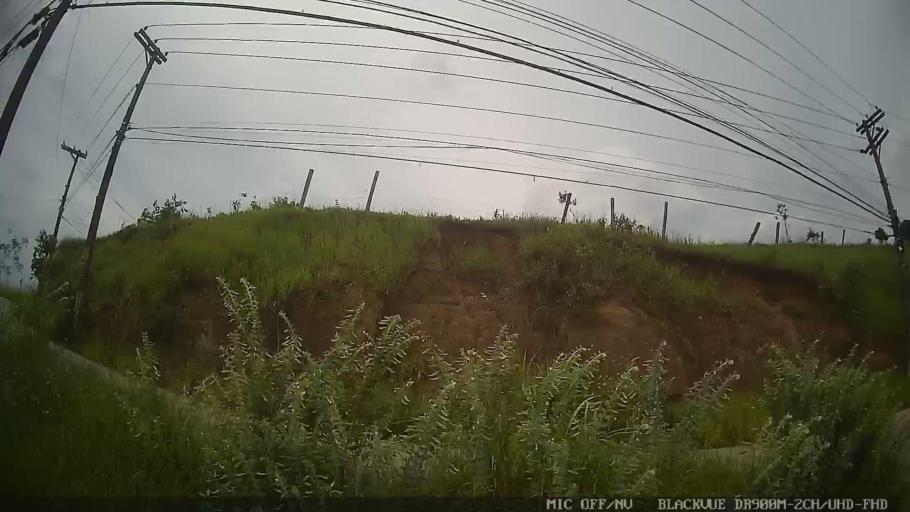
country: BR
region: Sao Paulo
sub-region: Aruja
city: Aruja
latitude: -23.4493
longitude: -46.2949
